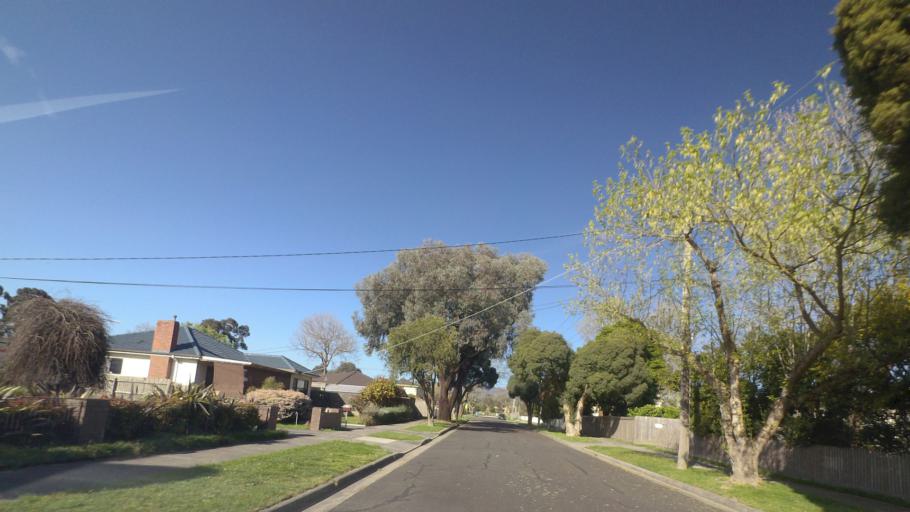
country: AU
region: Victoria
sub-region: Maroondah
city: Heathmont
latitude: -37.8374
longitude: 145.2596
